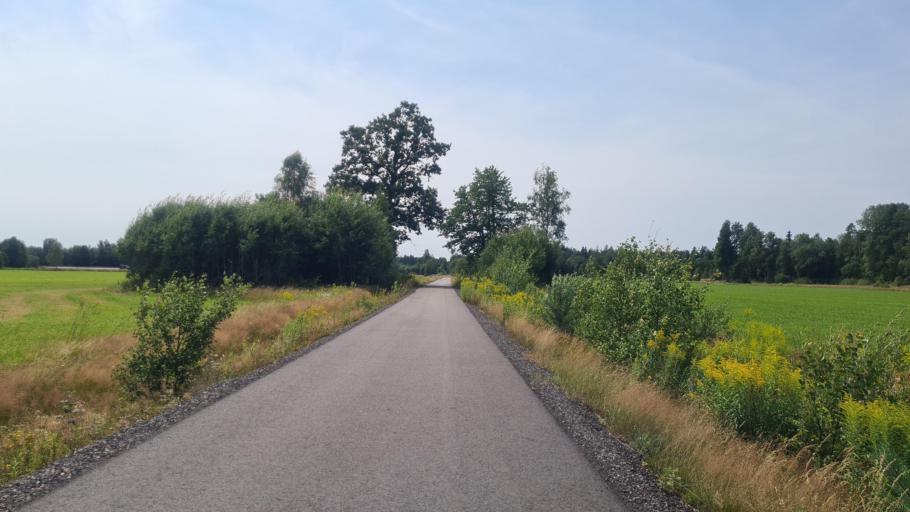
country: SE
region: Kronoberg
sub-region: Ljungby Kommun
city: Ljungby
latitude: 56.8549
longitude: 13.9728
